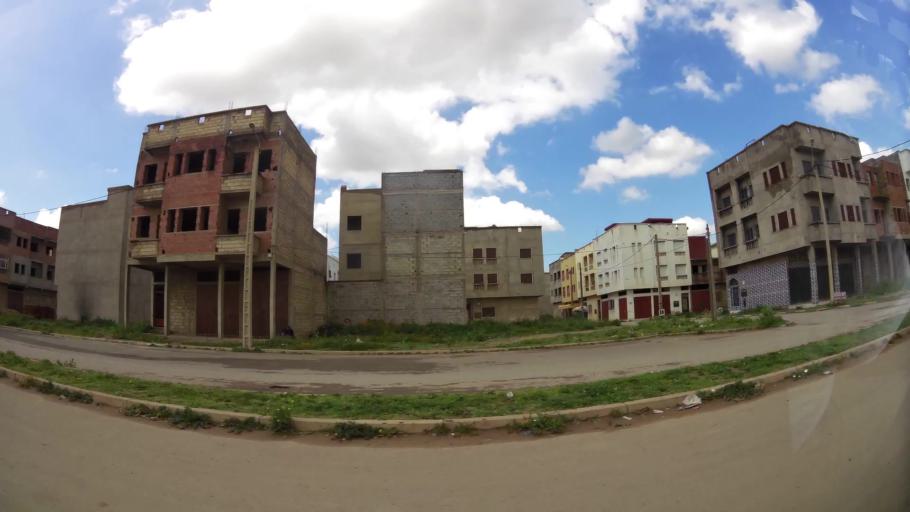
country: MA
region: Chaouia-Ouardigha
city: Nouaseur
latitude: 33.3620
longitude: -7.5344
